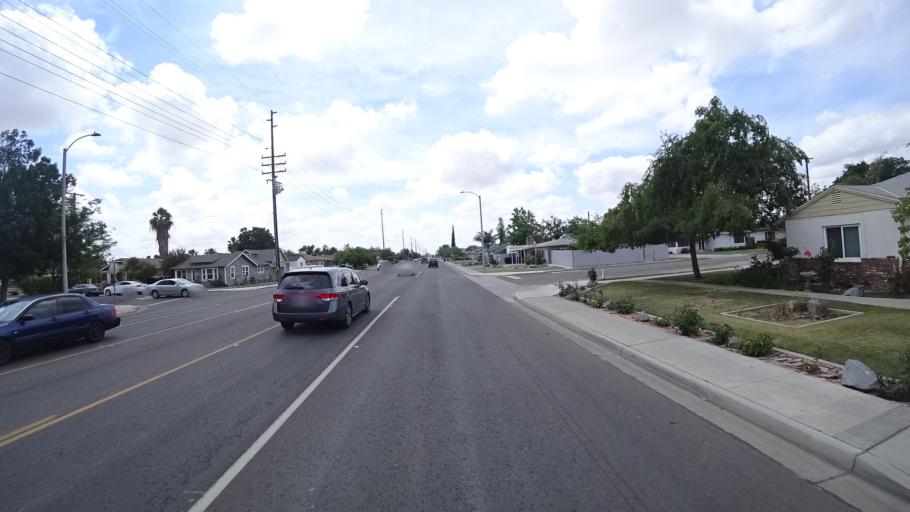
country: US
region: California
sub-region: Kings County
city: Hanford
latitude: 36.3393
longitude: -119.6552
